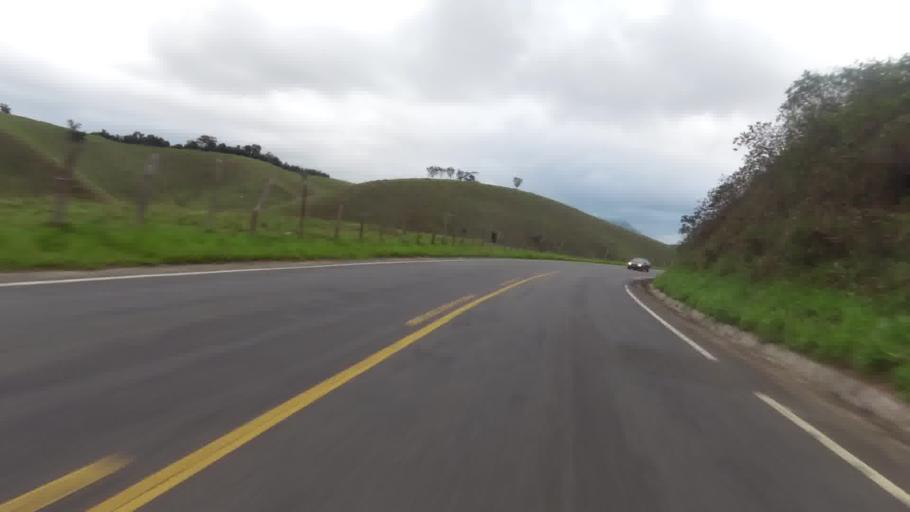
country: BR
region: Espirito Santo
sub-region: Alfredo Chaves
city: Alfredo Chaves
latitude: -20.6612
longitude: -40.7120
